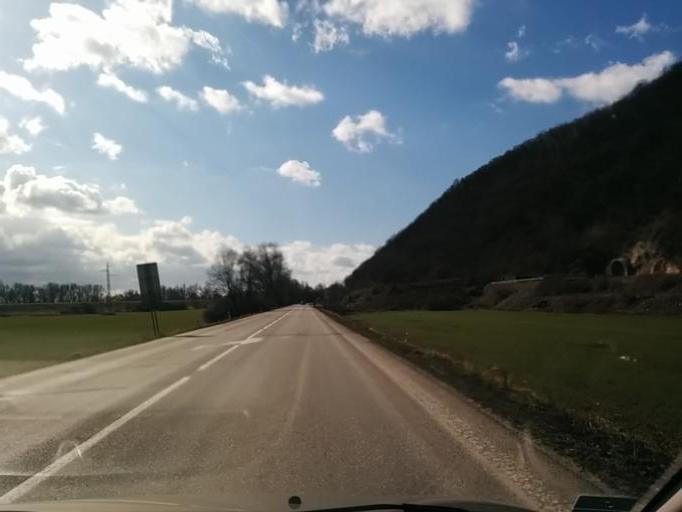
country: SK
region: Trenciansky
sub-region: Okres Nove Mesto nad Vahom
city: Nove Mesto nad Vahom
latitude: 48.7875
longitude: 17.8660
